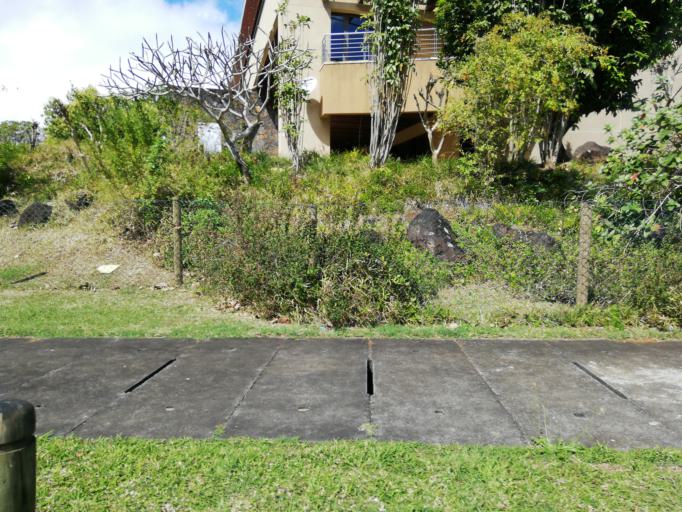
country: MU
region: Plaines Wilhems
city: Ebene
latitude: -20.2416
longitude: 57.4965
